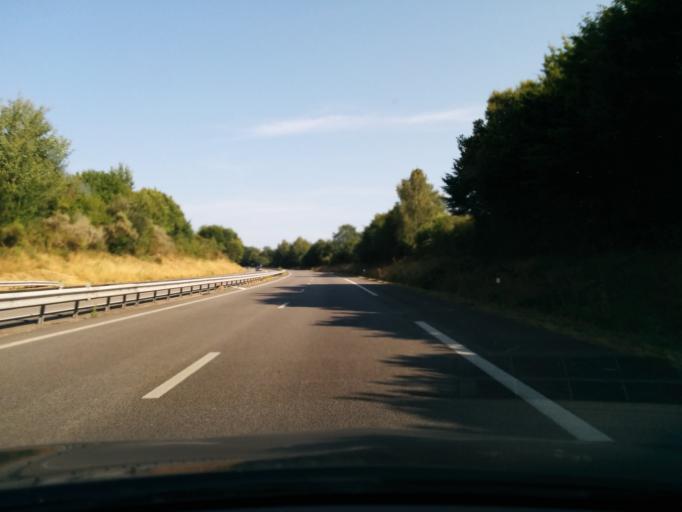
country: FR
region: Limousin
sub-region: Departement de la Haute-Vienne
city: Saint-Germain-les-Belles
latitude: 45.5959
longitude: 1.4509
